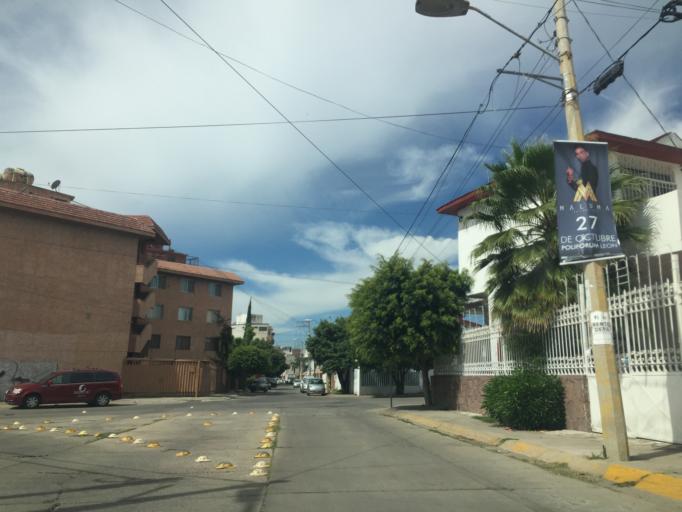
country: MX
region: Guanajuato
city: Leon
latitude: 21.1520
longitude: -101.6907
